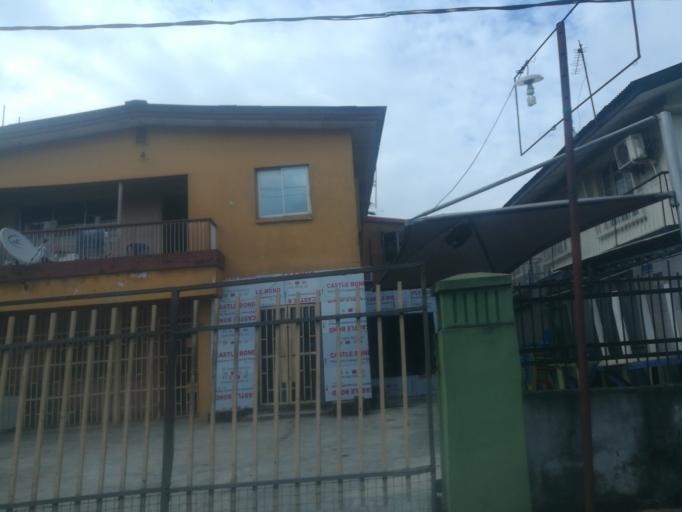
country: NG
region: Lagos
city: Somolu
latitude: 6.5492
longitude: 3.3701
